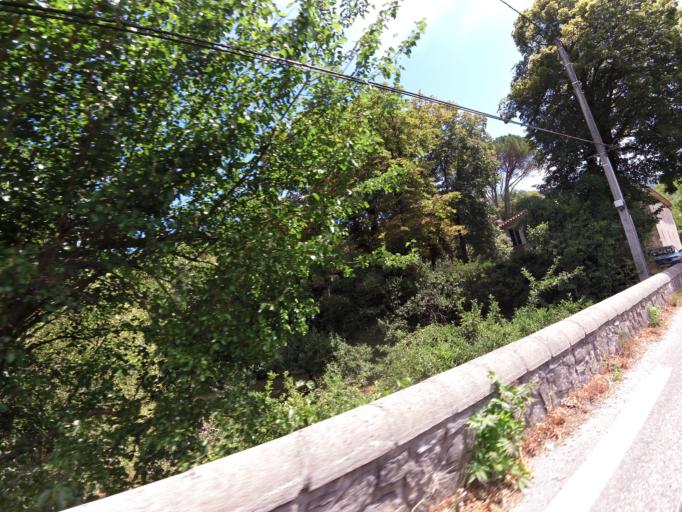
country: FR
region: Languedoc-Roussillon
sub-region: Departement du Gard
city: Sumene
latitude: 43.9742
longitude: 3.6869
